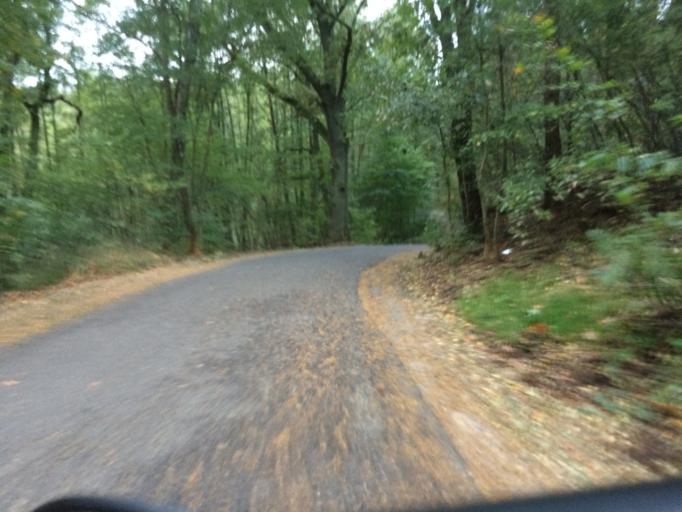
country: DE
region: Brandenburg
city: Birkenwerder
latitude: 52.7112
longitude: 13.2899
